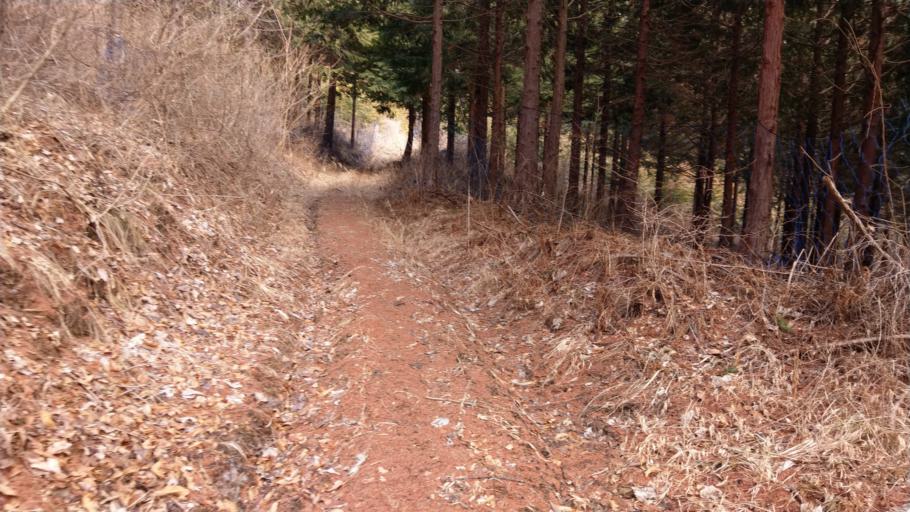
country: JP
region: Nagano
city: Komoro
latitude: 36.3745
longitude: 138.4418
